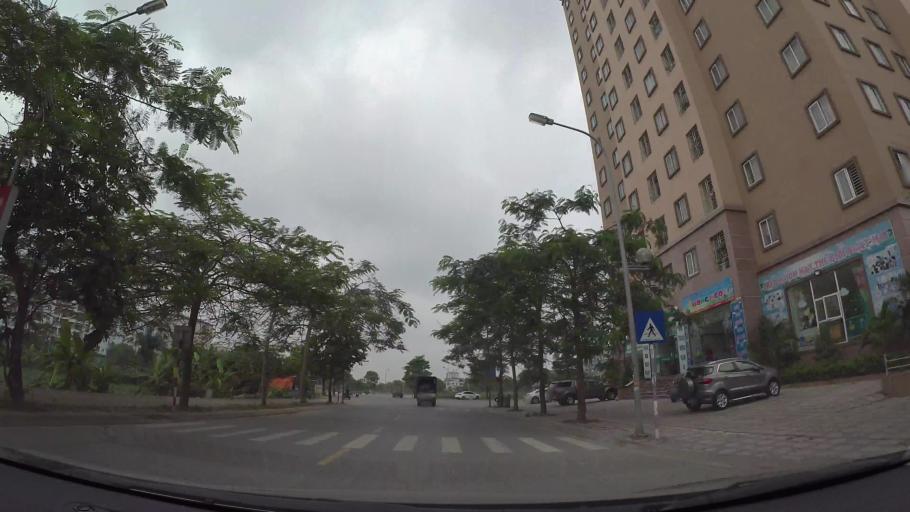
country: VN
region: Ha Noi
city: Trau Quy
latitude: 21.0586
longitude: 105.9148
